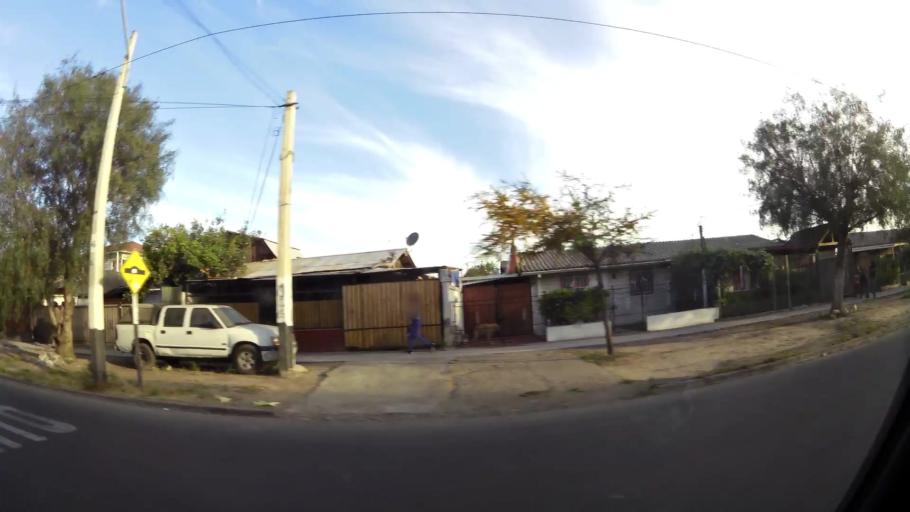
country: CL
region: Santiago Metropolitan
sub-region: Provincia de Santiago
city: Lo Prado
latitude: -33.4516
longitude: -70.7197
